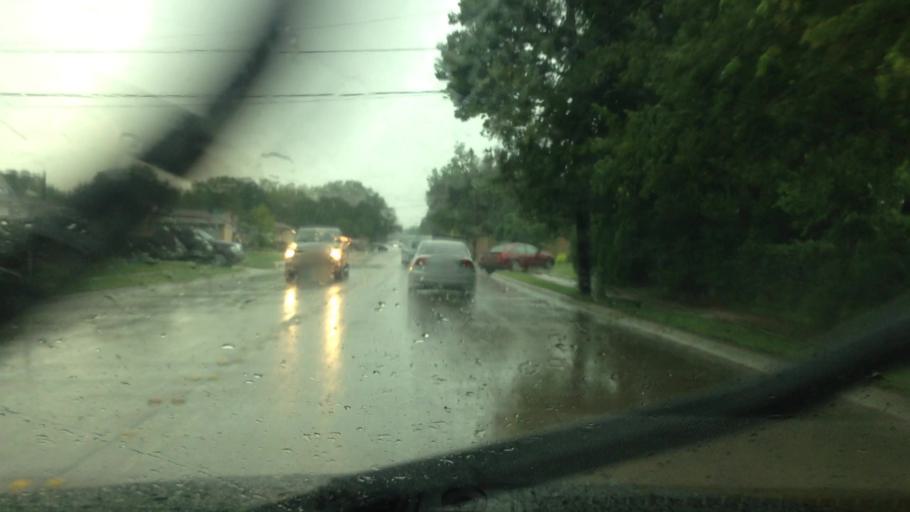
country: US
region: Texas
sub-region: Tarrant County
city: North Richland Hills
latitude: 32.8390
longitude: -97.2167
